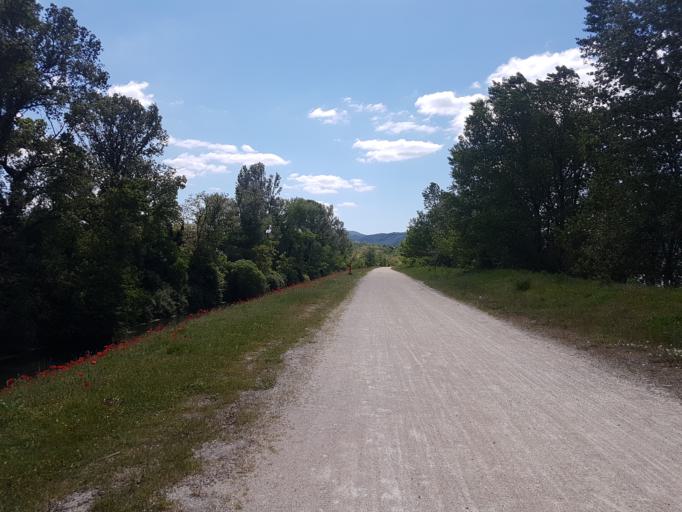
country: FR
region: Rhone-Alpes
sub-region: Departement de l'Ardeche
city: Mauves
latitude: 45.0474
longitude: 4.8573
